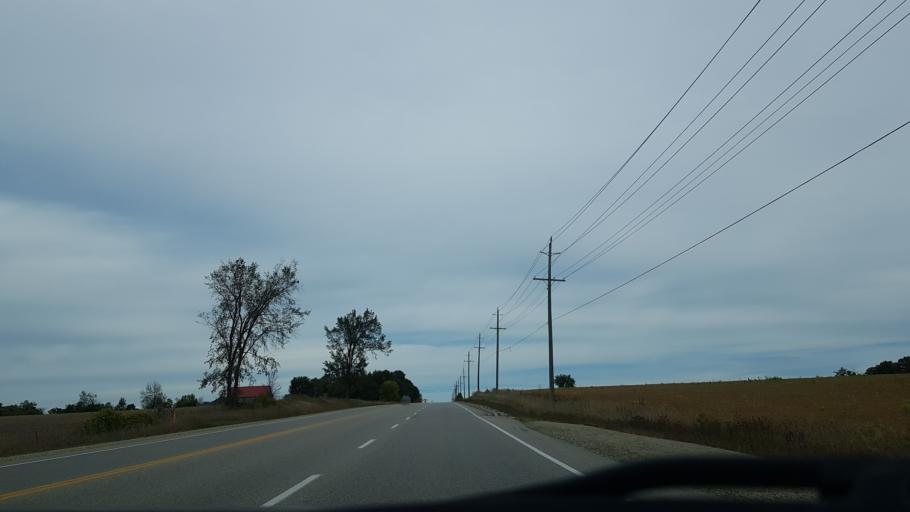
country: CA
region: Ontario
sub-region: Wellington County
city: Guelph
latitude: 43.6544
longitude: -80.1801
